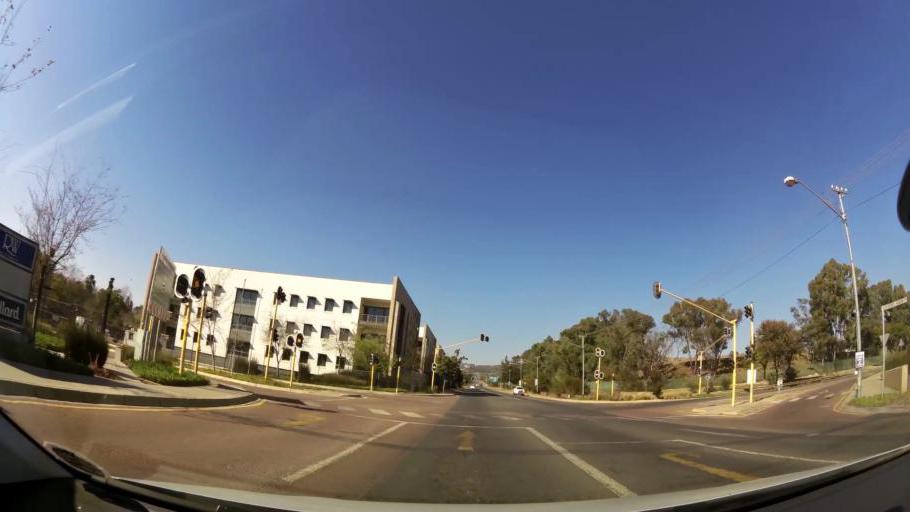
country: ZA
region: Gauteng
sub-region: City of Tshwane Metropolitan Municipality
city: Pretoria
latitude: -25.7665
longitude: 28.2216
